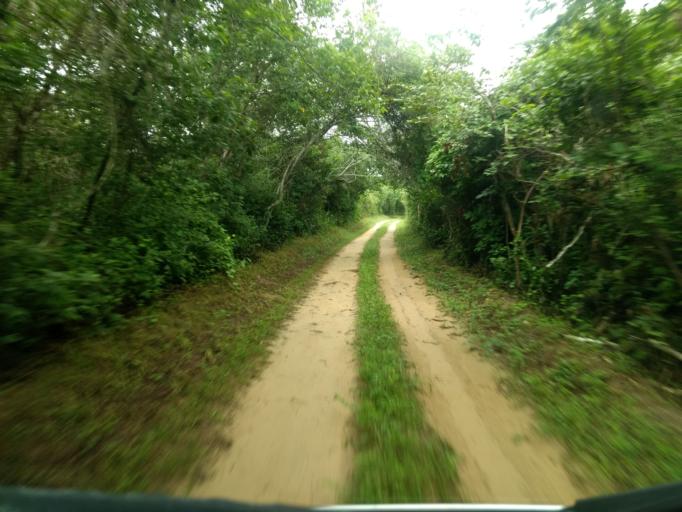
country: BR
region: Ceara
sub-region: Crateus
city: Crateus
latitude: -5.1572
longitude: -40.9208
